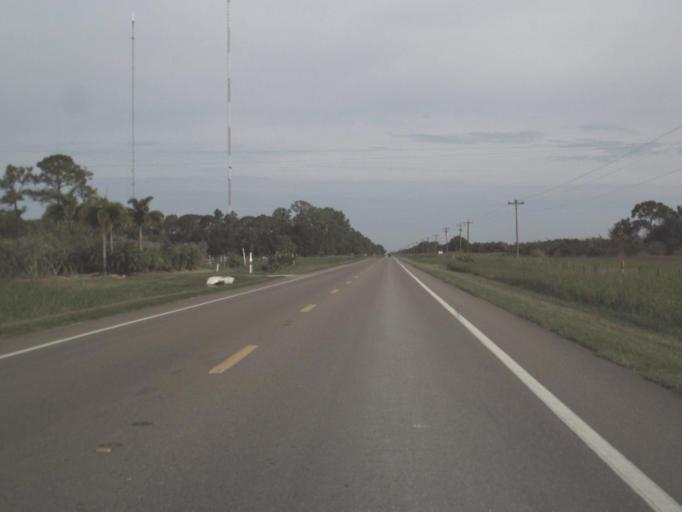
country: US
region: Florida
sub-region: Lee County
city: Fort Myers Shores
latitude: 26.8065
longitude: -81.7603
